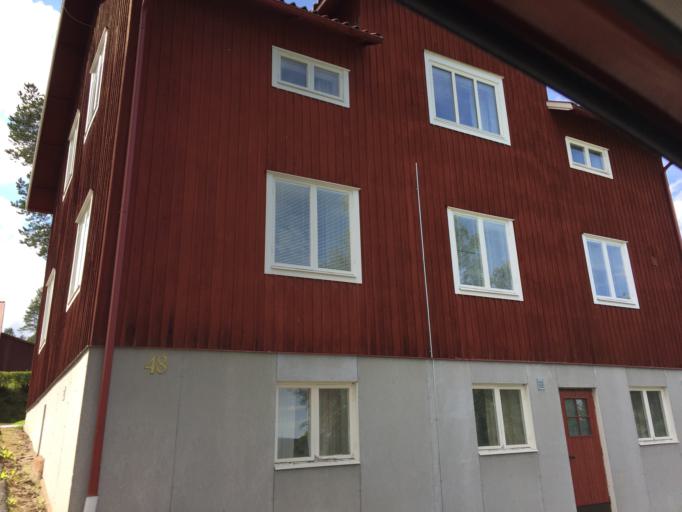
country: SE
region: Gaevleborg
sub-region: Ljusdals Kommun
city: Jaervsoe
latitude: 61.7403
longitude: 16.1631
